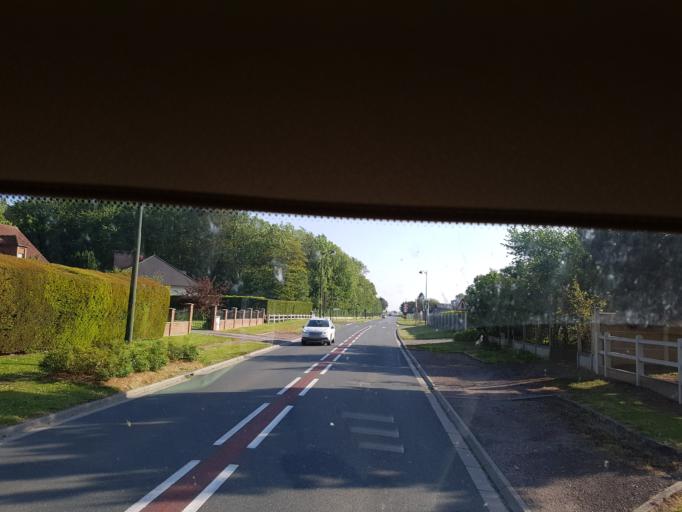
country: FR
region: Picardie
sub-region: Departement de la Somme
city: Abbeville
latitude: 50.1525
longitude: 1.8525
